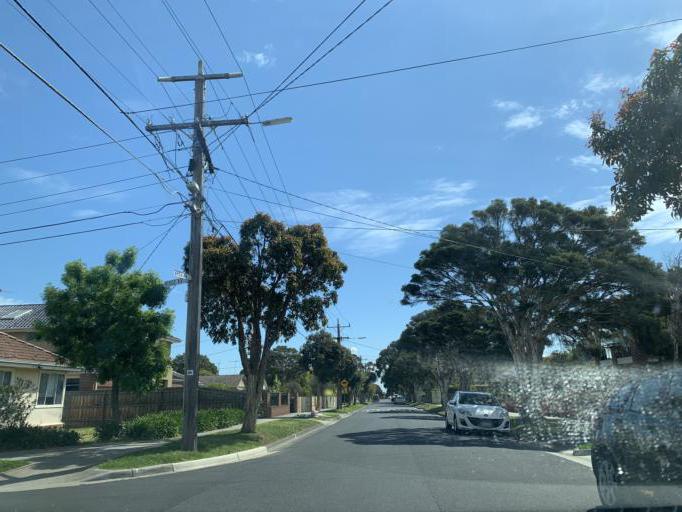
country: AU
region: Victoria
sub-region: Bayside
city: Hampton East
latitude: -37.9379
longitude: 145.0262
